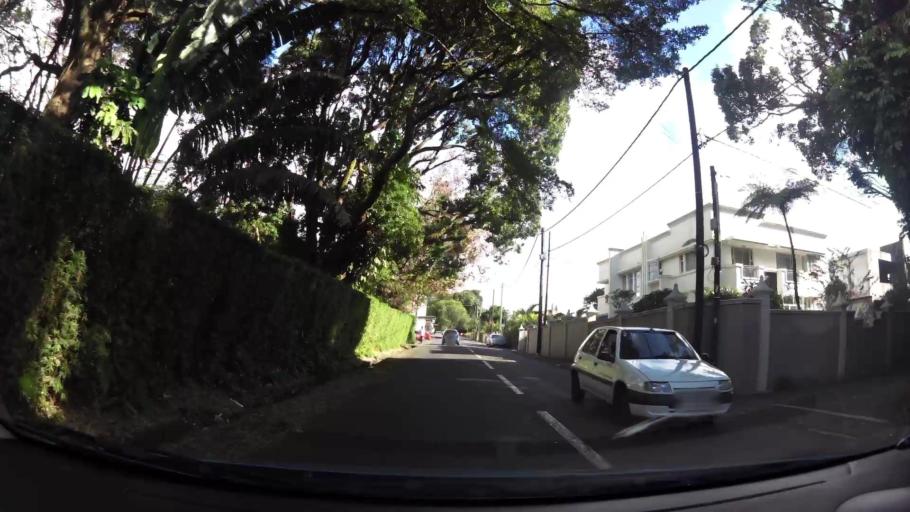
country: MU
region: Plaines Wilhems
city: Curepipe
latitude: -20.3223
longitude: 57.5188
